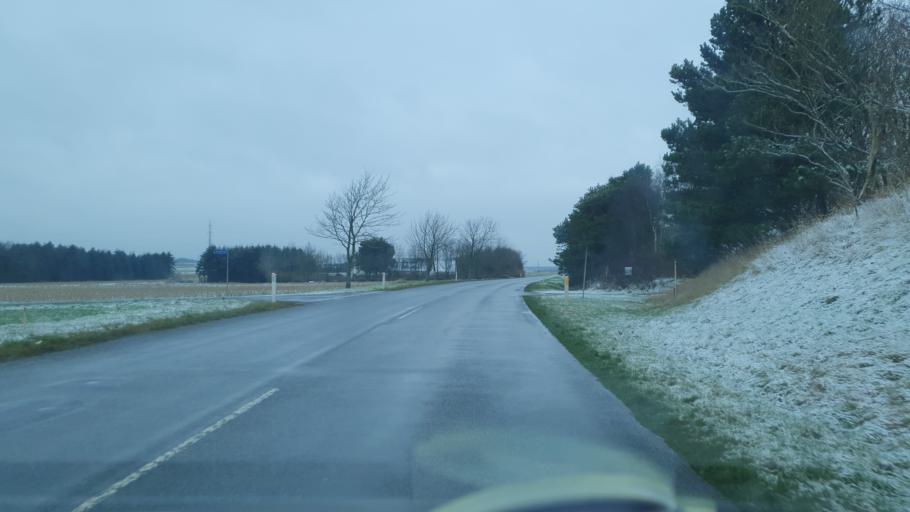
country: DK
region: North Denmark
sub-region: Jammerbugt Kommune
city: Brovst
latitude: 57.1098
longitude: 9.5008
